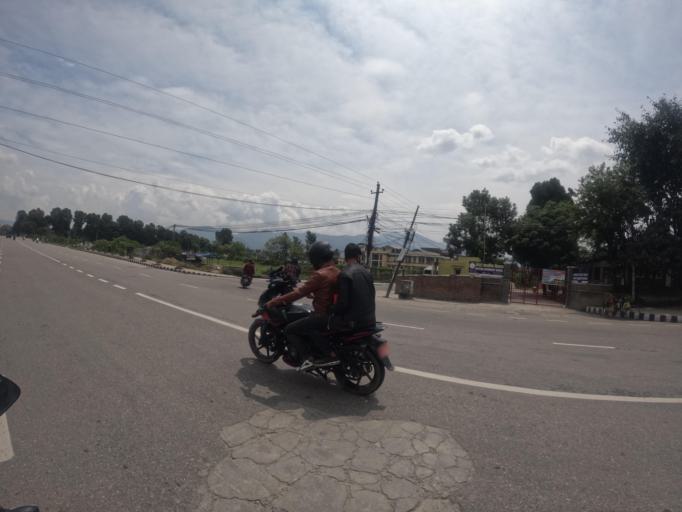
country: NP
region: Central Region
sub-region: Bagmati Zone
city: Bhaktapur
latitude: 27.6822
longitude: 85.3769
